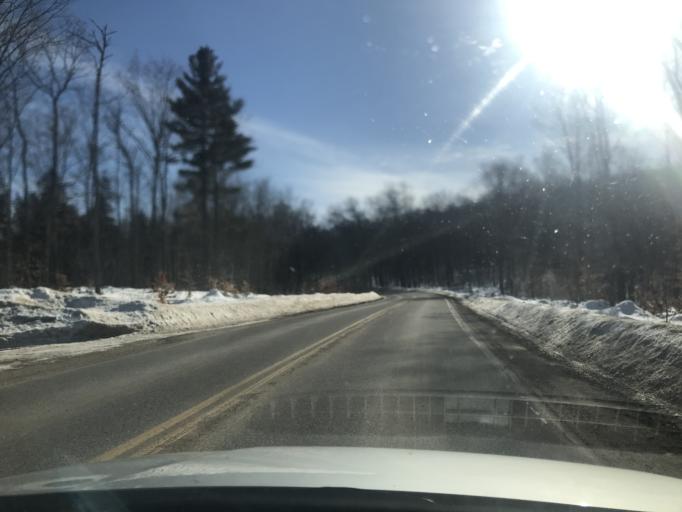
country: US
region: Michigan
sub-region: Dickinson County
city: Kingsford
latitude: 45.4091
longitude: -88.3522
